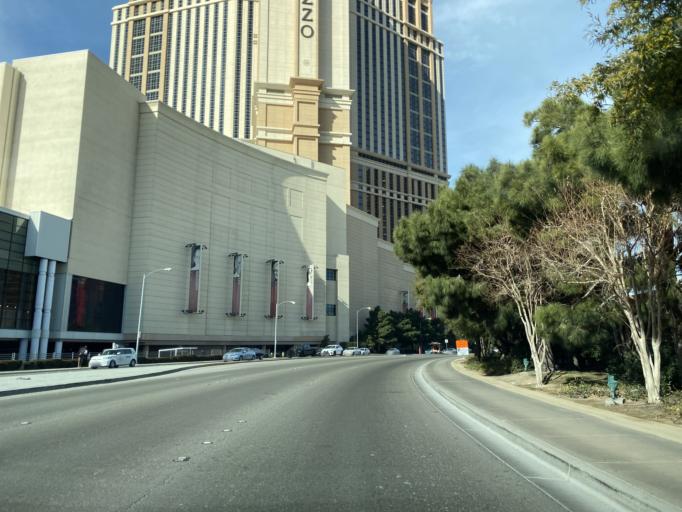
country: US
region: Nevada
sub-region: Clark County
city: Paradise
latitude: 36.1227
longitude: -115.1656
